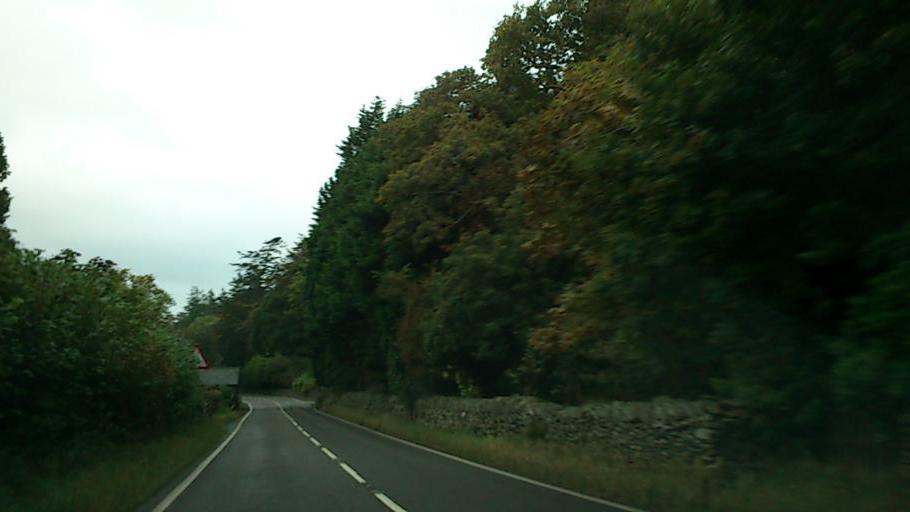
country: GB
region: Wales
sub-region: Sir Powys
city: Machynlleth
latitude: 52.5468
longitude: -3.9356
